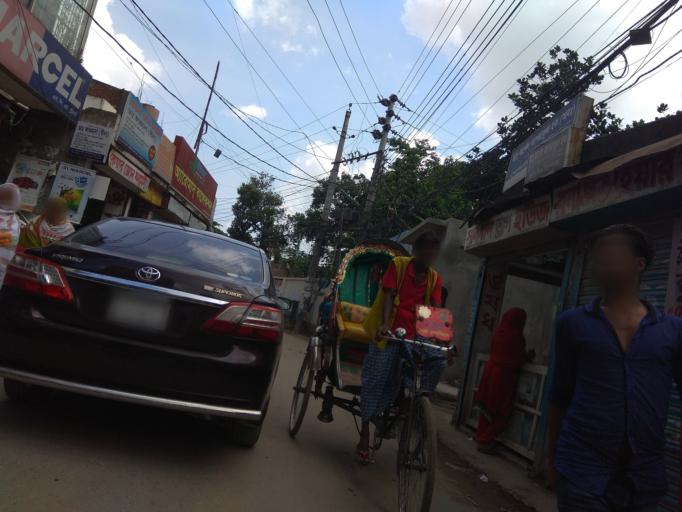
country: BD
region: Dhaka
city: Tungi
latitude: 23.8271
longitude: 90.3933
